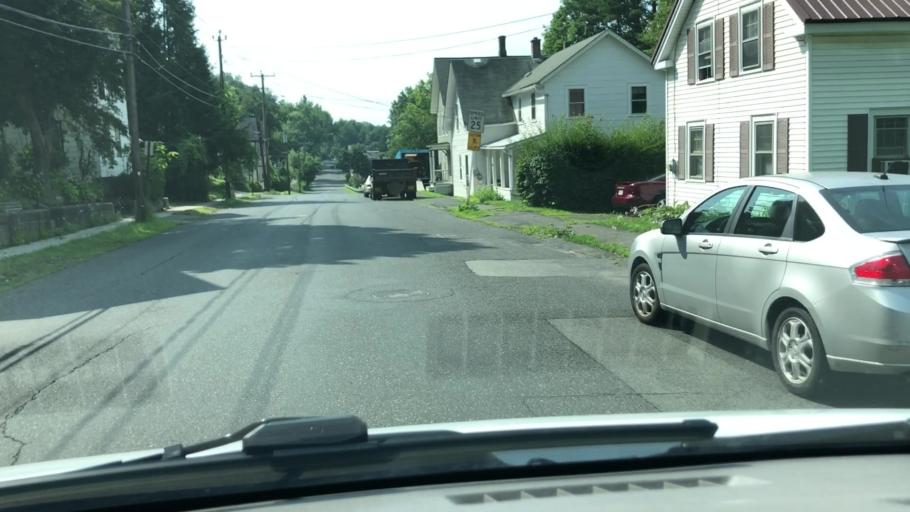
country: US
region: Massachusetts
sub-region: Franklin County
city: Greenfield
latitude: 42.5823
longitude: -72.5978
